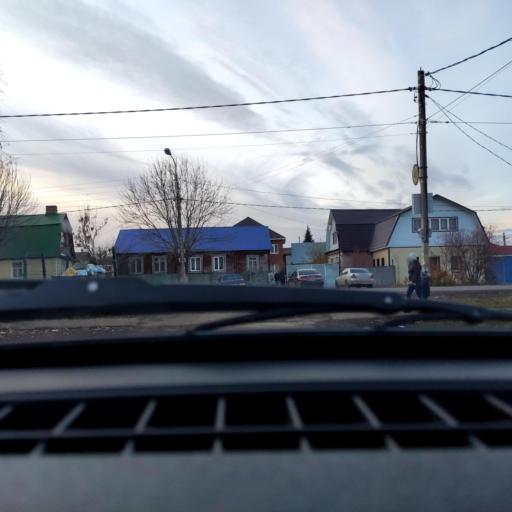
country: RU
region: Bashkortostan
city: Ufa
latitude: 54.7377
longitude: 55.9213
